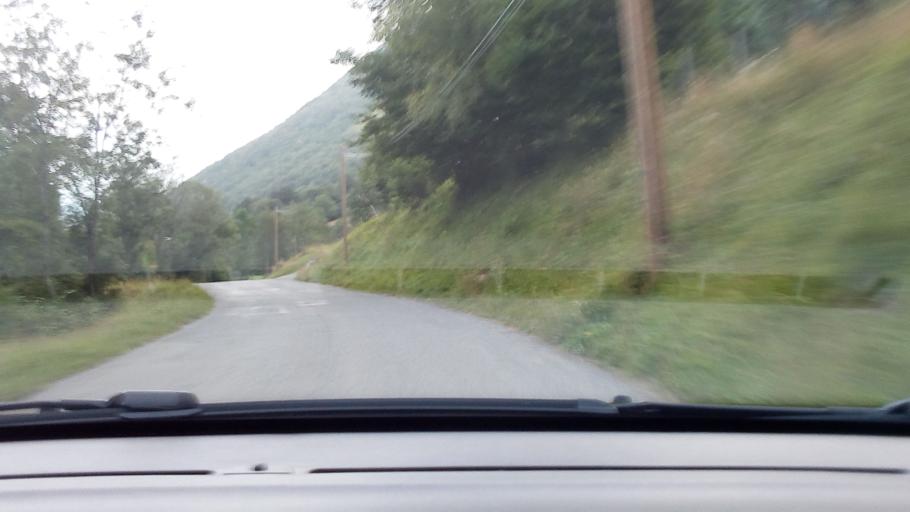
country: FR
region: Midi-Pyrenees
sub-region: Departement des Hautes-Pyrenees
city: Cauterets
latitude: 42.9263
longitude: -0.1828
